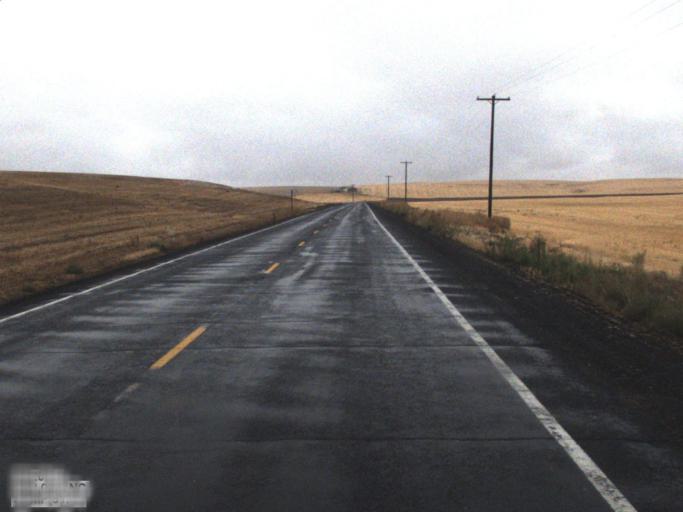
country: US
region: Washington
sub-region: Lincoln County
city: Davenport
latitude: 47.4648
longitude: -118.1841
